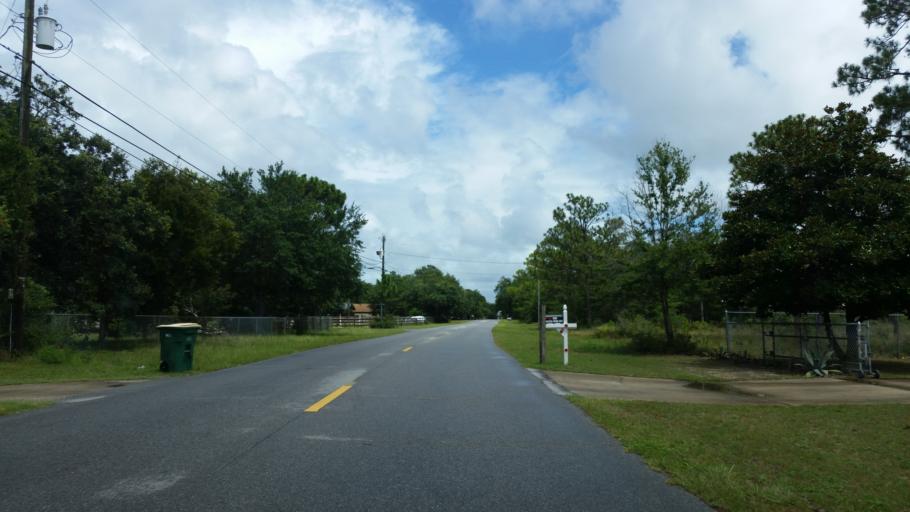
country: US
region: Florida
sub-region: Santa Rosa County
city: Navarre
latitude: 30.4324
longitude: -86.8579
